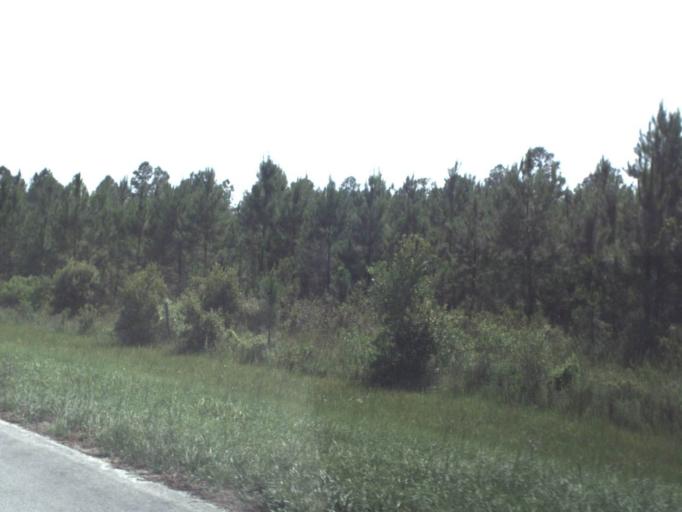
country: US
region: Florida
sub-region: Baker County
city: Macclenny
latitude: 30.1876
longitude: -82.1663
